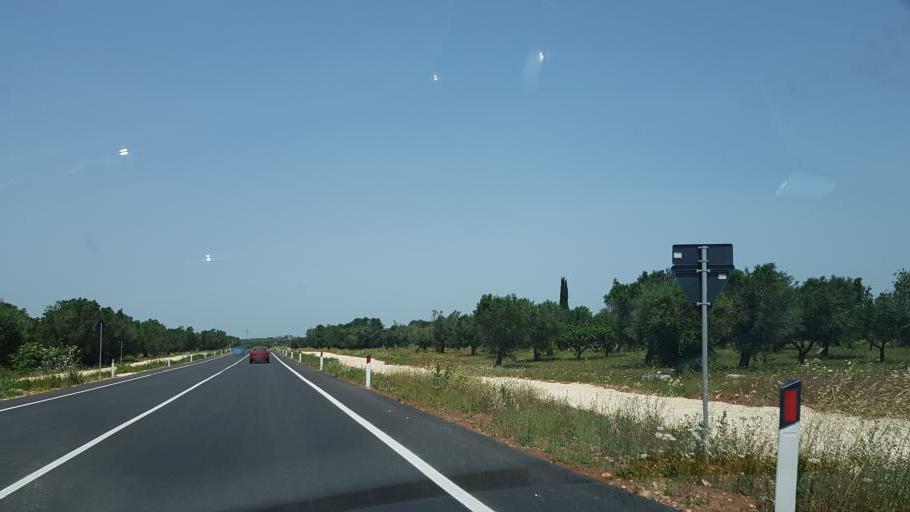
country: IT
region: Apulia
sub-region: Provincia di Brindisi
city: San Pancrazio Salentino
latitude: 40.4702
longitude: 17.8381
